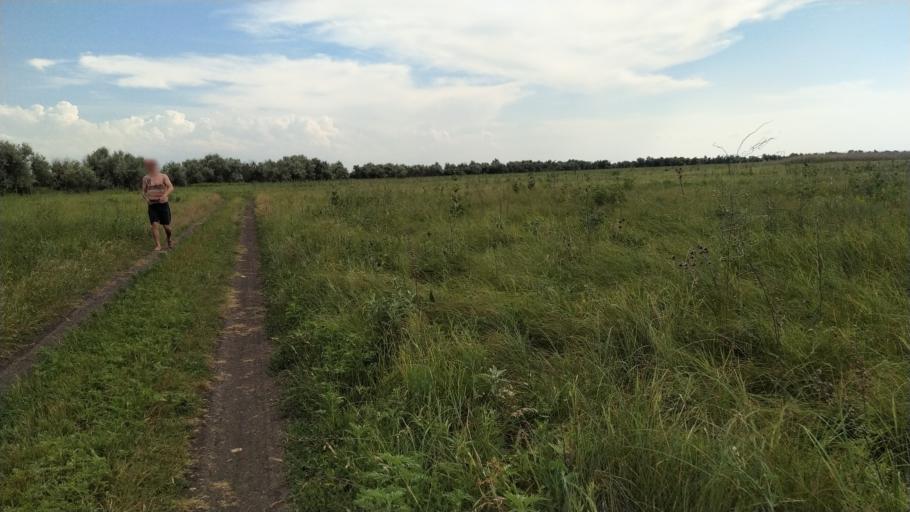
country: RU
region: Rostov
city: Kuleshovka
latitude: 47.1268
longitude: 39.6289
